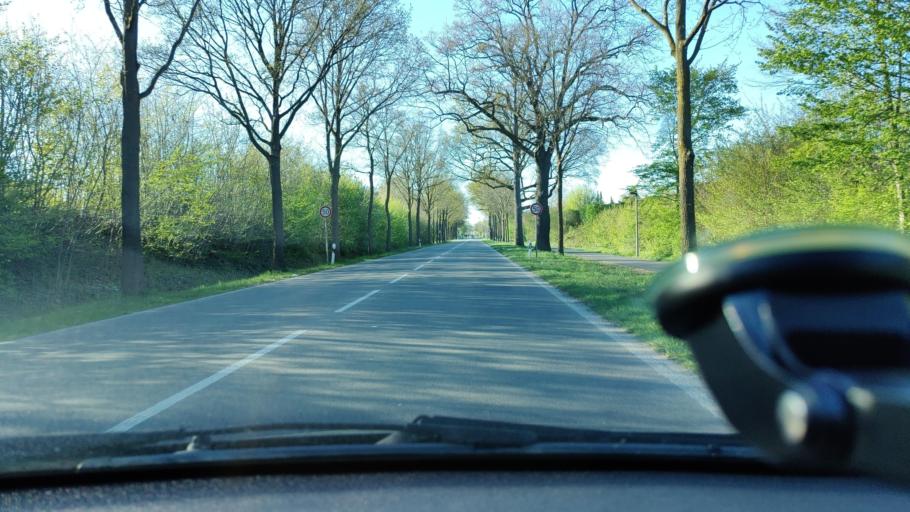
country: DE
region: North Rhine-Westphalia
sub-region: Regierungsbezirk Munster
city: Legden
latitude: 52.0337
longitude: 7.0953
